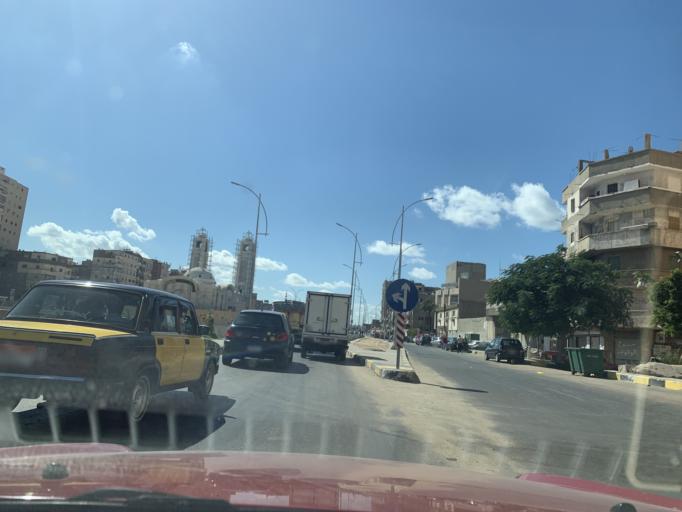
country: EG
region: Alexandria
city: Alexandria
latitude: 31.2231
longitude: 29.9720
